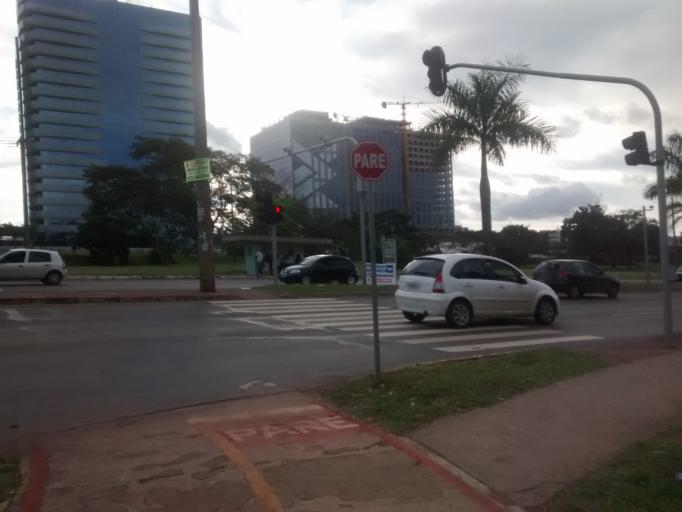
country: BR
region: Federal District
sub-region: Brasilia
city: Brasilia
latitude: -15.7862
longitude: -47.8734
